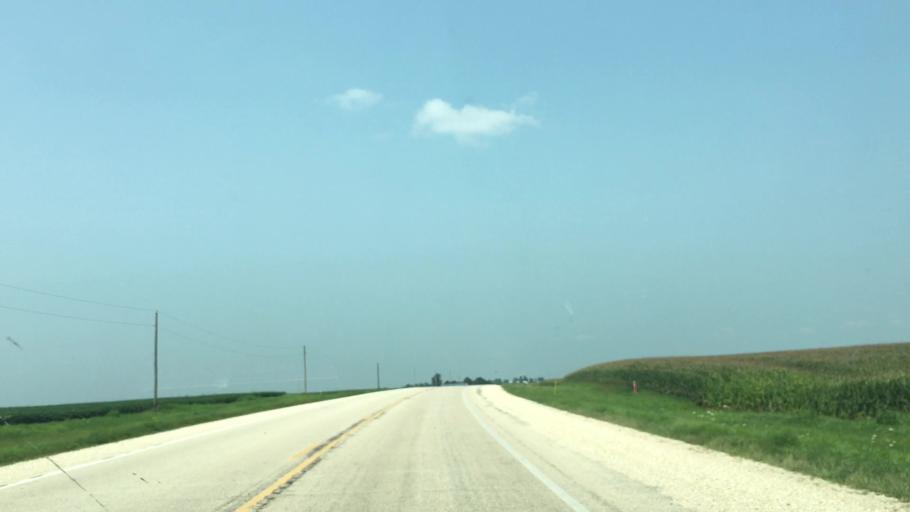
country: US
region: Iowa
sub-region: Fayette County
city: West Union
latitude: 42.9820
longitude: -91.8243
